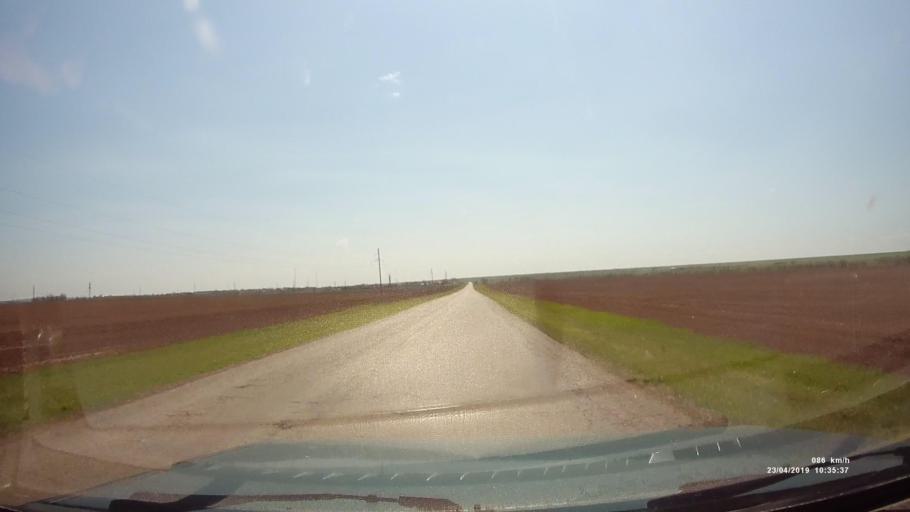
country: RU
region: Kalmykiya
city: Yashalta
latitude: 46.5522
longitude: 42.6264
